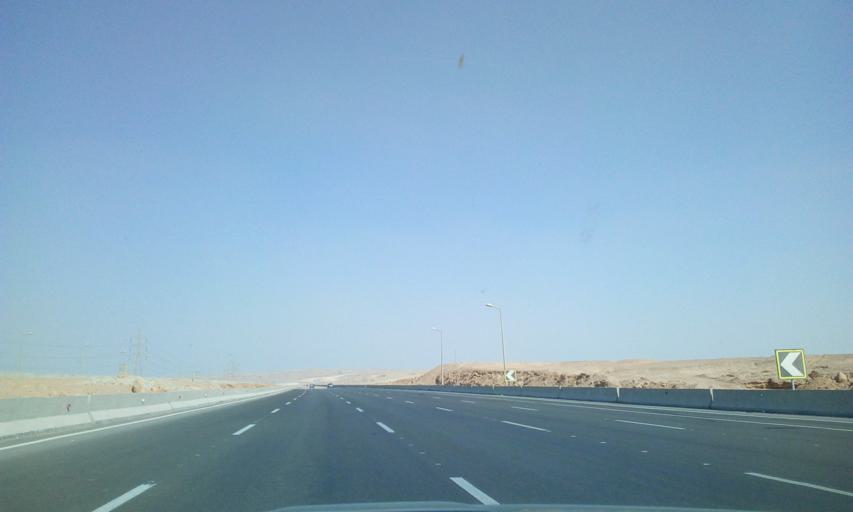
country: EG
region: As Suways
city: Ain Sukhna
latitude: 29.7632
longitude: 31.9621
